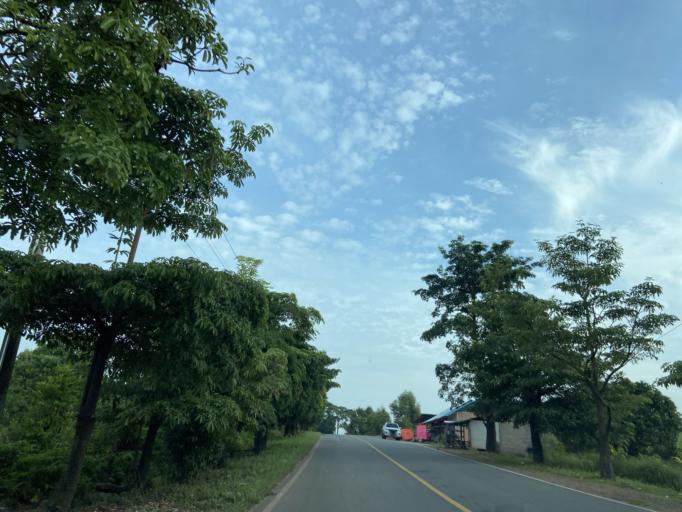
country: ID
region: Riau Islands
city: Tanjungpinang
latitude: 0.9256
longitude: 104.1156
